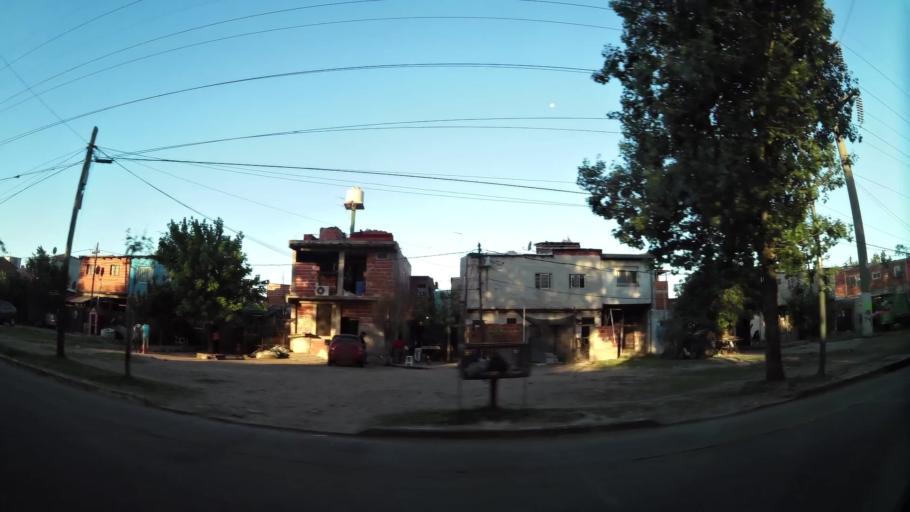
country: AR
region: Buenos Aires
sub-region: Partido de Tigre
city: Tigre
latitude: -34.4446
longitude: -58.5759
